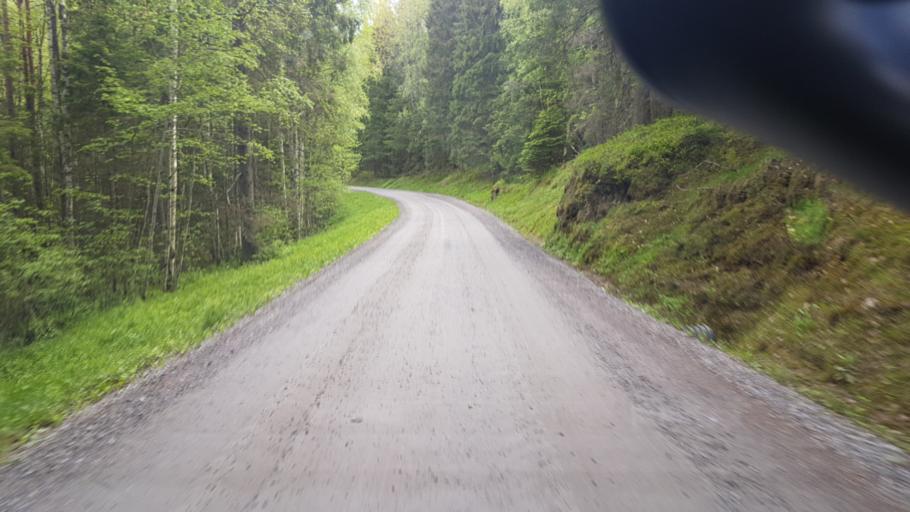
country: NO
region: Ostfold
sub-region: Romskog
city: Romskog
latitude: 59.7016
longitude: 11.9490
